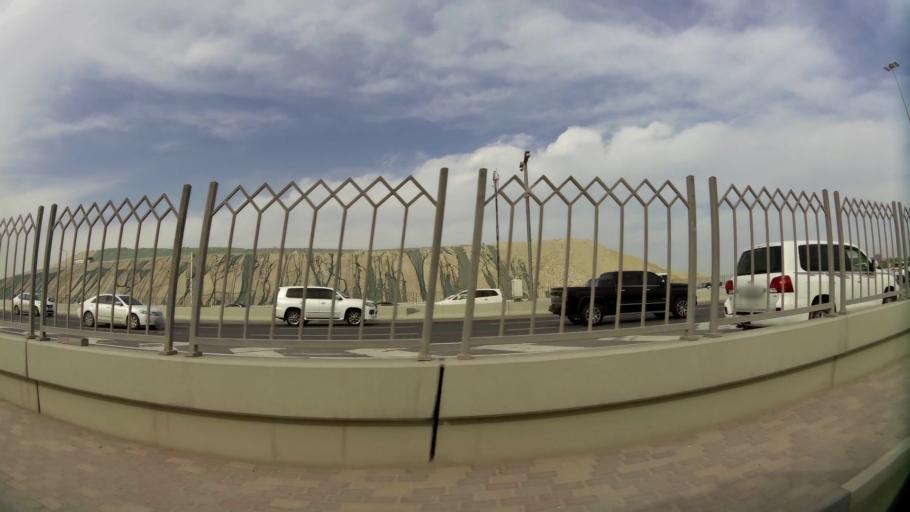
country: QA
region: Baladiyat ad Dawhah
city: Doha
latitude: 25.2887
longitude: 51.4792
